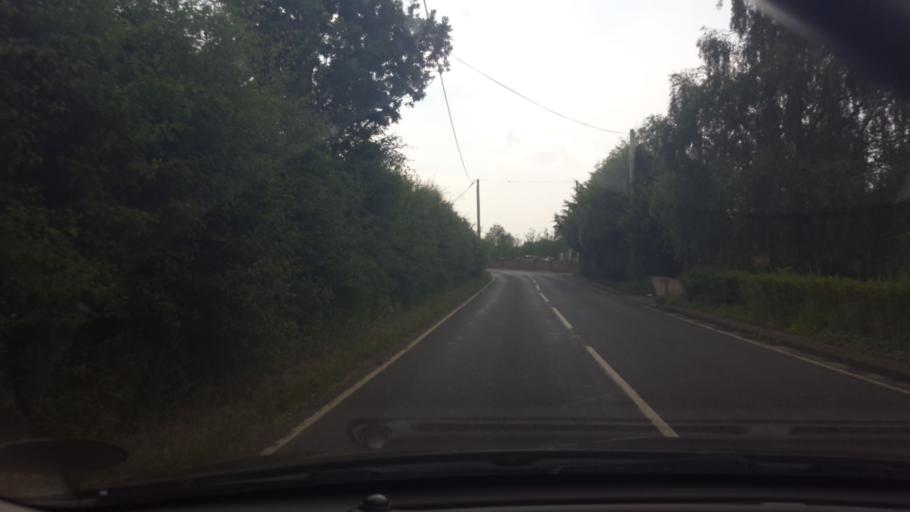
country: GB
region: England
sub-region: Essex
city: Mistley
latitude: 51.8943
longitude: 1.1021
